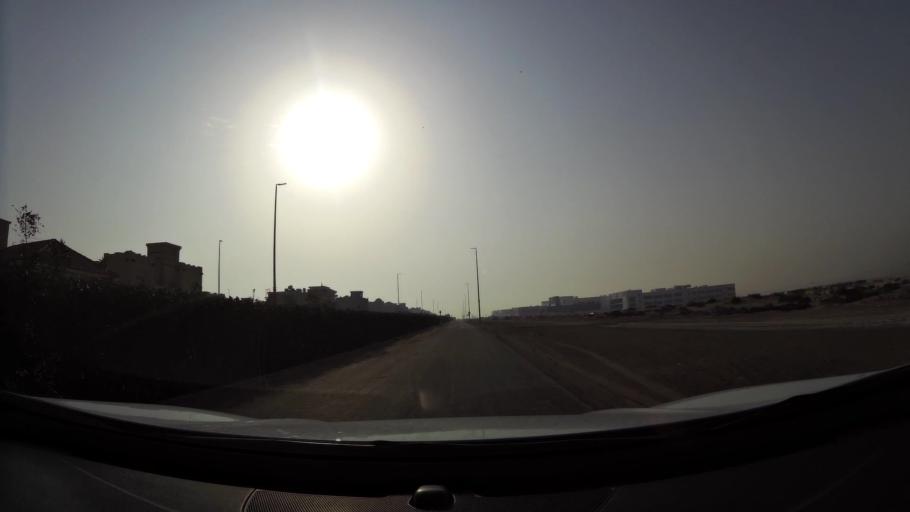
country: AE
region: Abu Dhabi
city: Abu Dhabi
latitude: 24.2979
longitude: 54.6155
